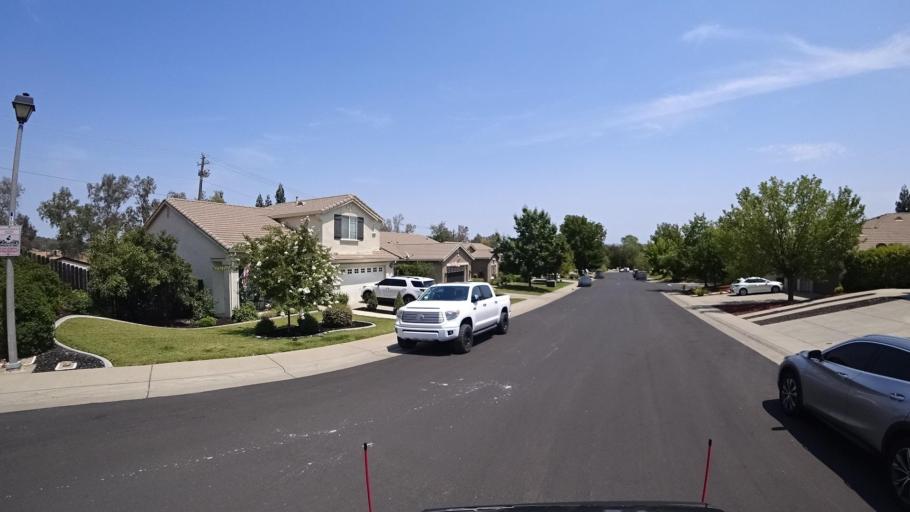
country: US
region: California
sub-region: Placer County
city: Rocklin
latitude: 38.8100
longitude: -121.2262
